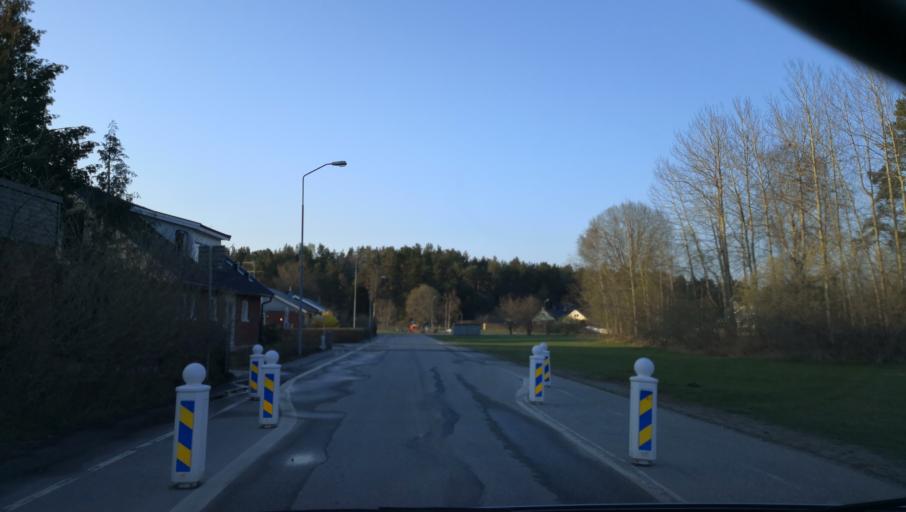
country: SE
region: Stockholm
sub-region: Varmdo Kommun
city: Hemmesta
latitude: 59.3210
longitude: 18.5062
